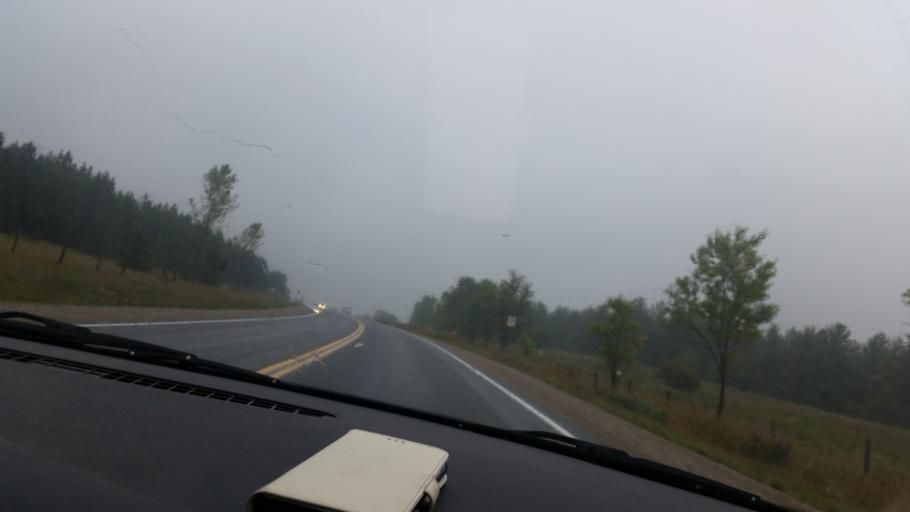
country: CA
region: Ontario
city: Stratford
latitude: 43.2590
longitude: -81.0773
